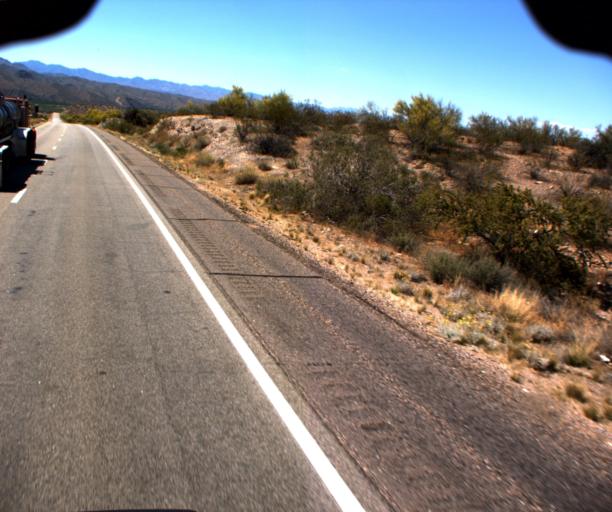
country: US
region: Arizona
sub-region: Yavapai County
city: Bagdad
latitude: 34.6294
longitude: -113.5416
